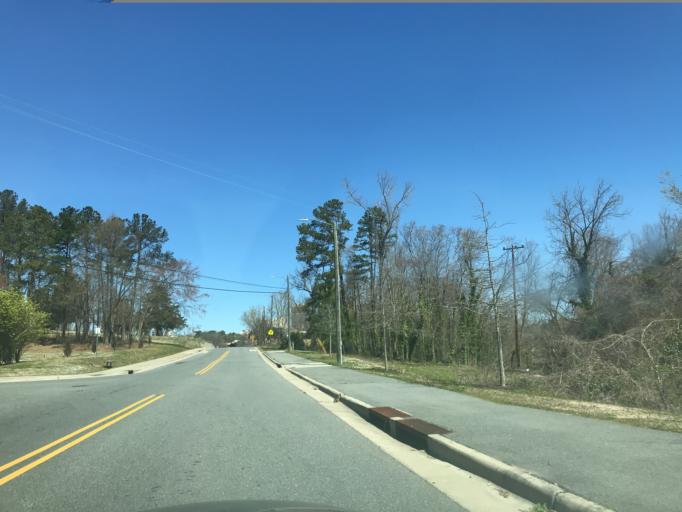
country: US
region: North Carolina
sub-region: Wake County
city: Raleigh
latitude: 35.7626
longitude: -78.6439
